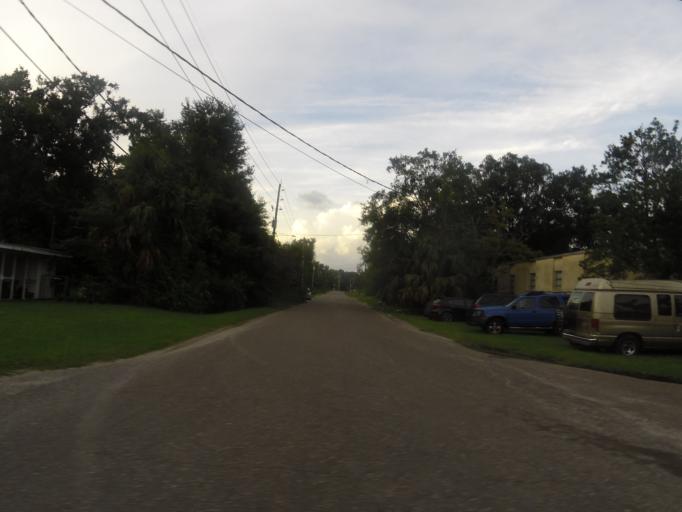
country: US
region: Florida
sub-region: Duval County
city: Jacksonville
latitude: 30.3516
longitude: -81.7163
